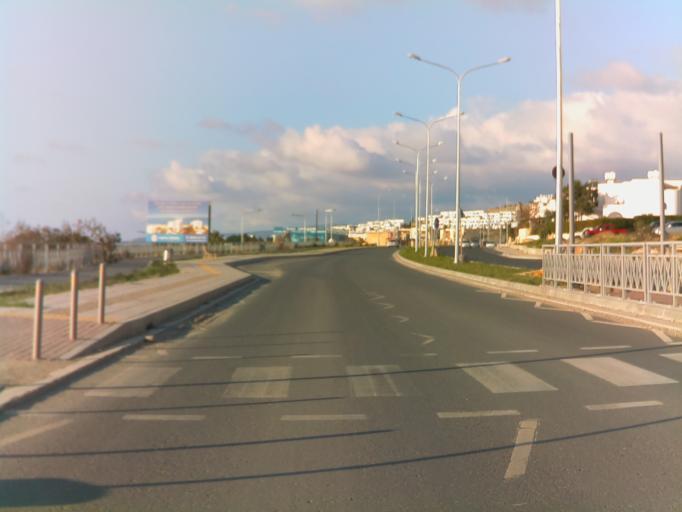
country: CY
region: Pafos
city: Chlorakas
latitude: 34.7804
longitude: 32.4060
